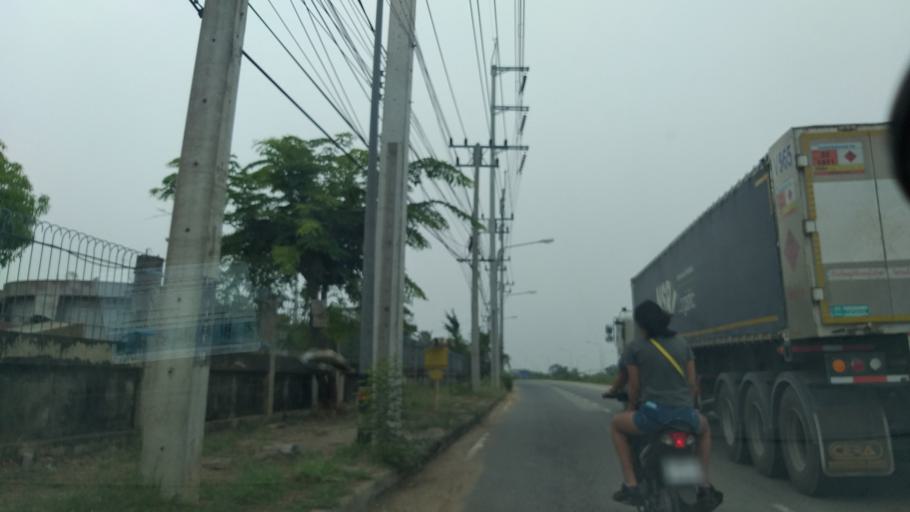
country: TH
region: Chon Buri
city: Ko Chan
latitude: 13.4747
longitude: 101.2838
